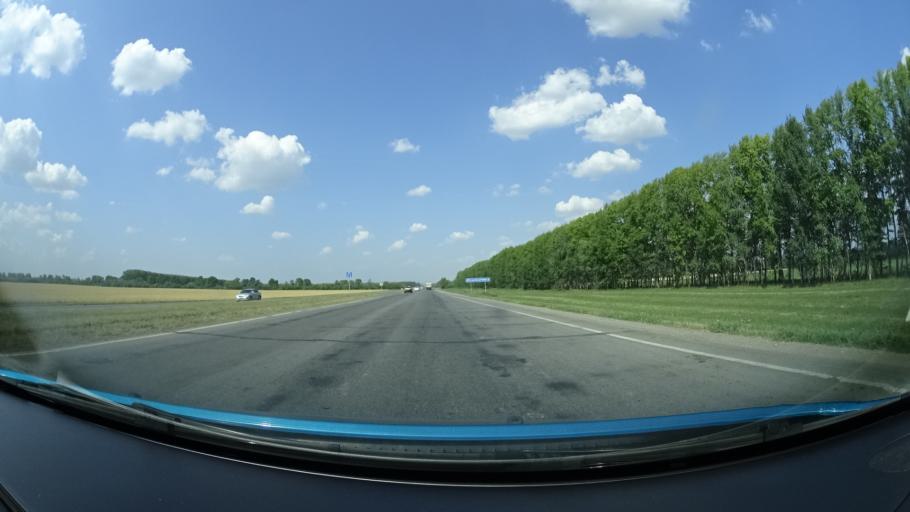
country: RU
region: Bashkortostan
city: Chishmy
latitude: 54.6567
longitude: 55.4775
